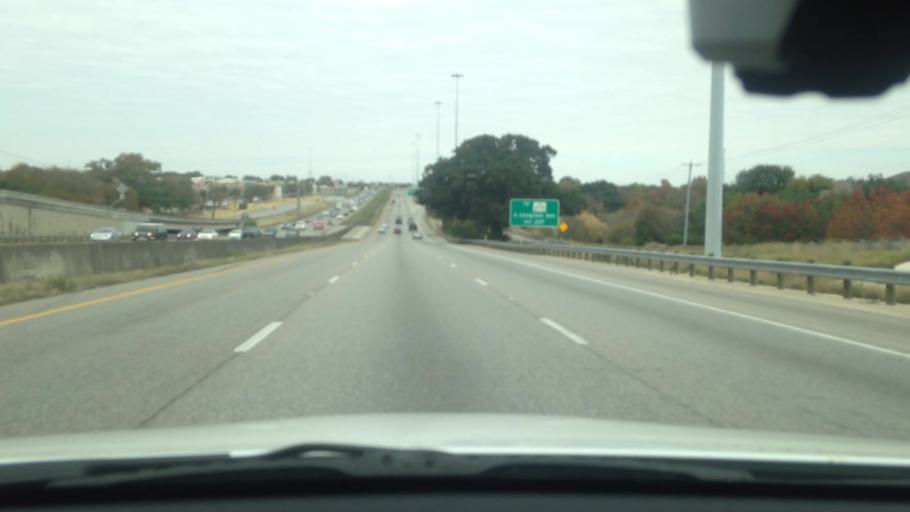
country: US
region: Texas
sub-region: Travis County
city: Onion Creek
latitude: 30.1509
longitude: -97.7921
